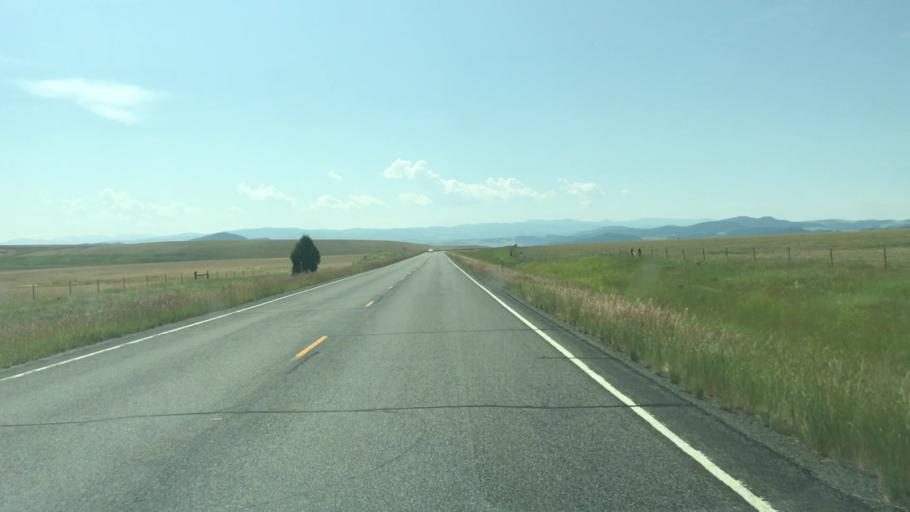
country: US
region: Montana
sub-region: Lewis and Clark County
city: Lincoln
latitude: 46.6829
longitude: -112.6545
